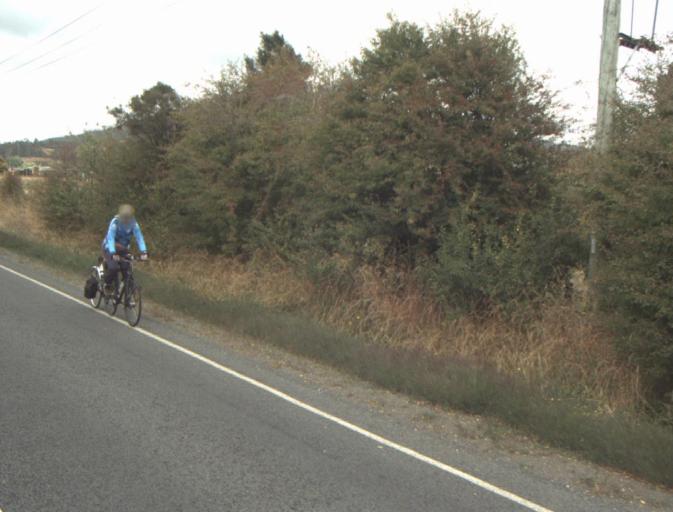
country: AU
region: Tasmania
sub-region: Launceston
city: Mayfield
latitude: -41.2433
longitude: 147.2167
